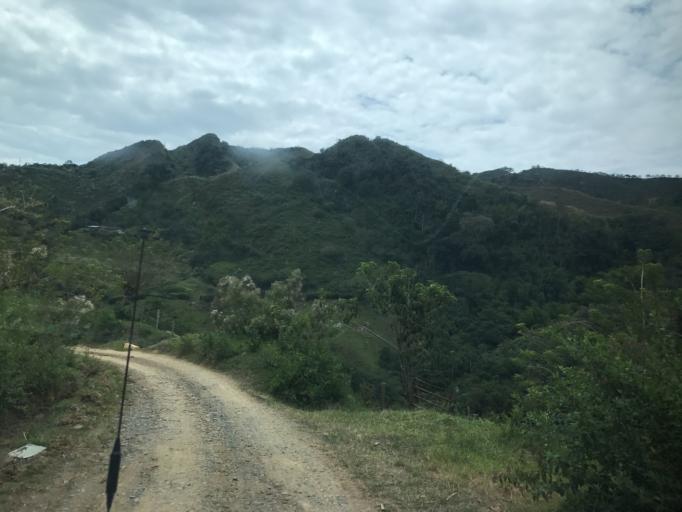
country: CO
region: Valle del Cauca
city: Obando
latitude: 4.5518
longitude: -75.9142
